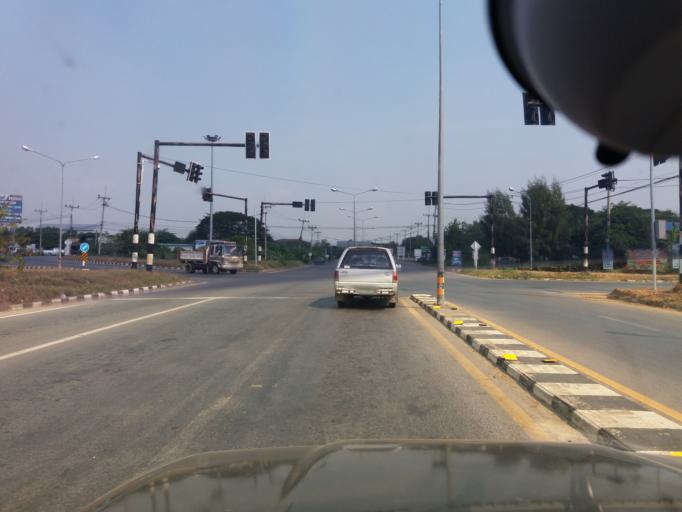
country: TH
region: Sing Buri
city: Sing Buri
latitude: 14.8859
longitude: 100.3904
